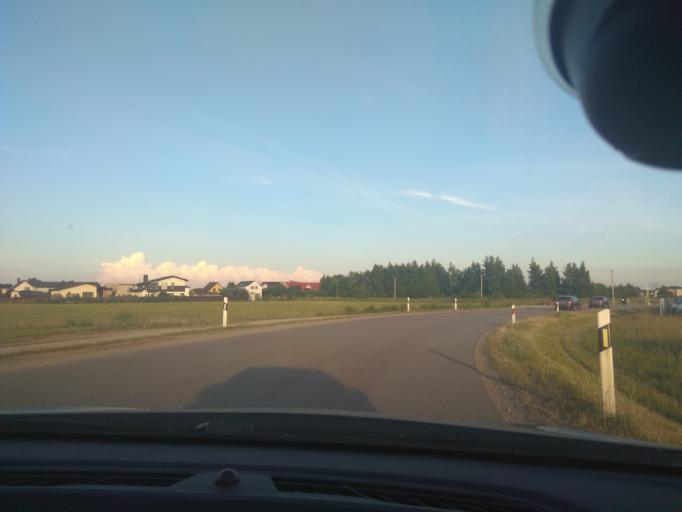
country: LT
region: Klaipedos apskritis
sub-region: Klaipeda
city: Klaipeda
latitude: 55.7551
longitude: 21.1737
